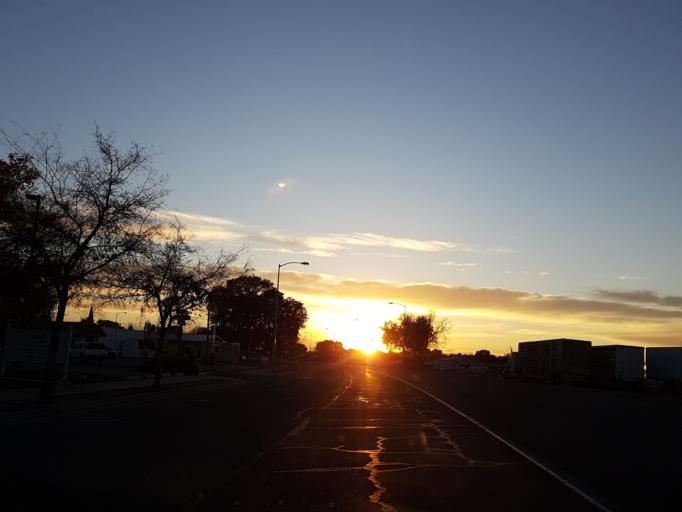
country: US
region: Oregon
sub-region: Malheur County
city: Vale
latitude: 43.9827
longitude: -117.2474
